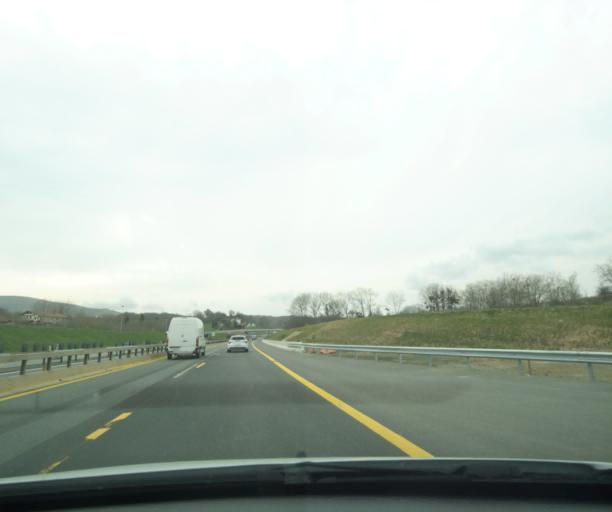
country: FR
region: Aquitaine
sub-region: Departement des Pyrenees-Atlantiques
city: Urrugne
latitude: 43.3609
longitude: -1.6948
